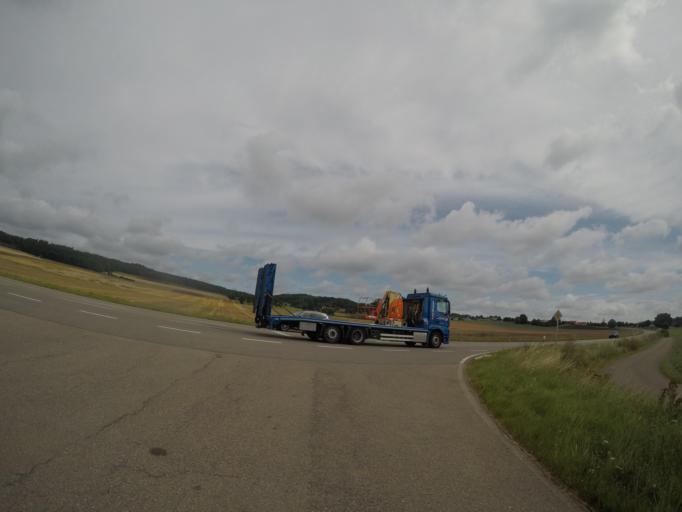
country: DE
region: Baden-Wuerttemberg
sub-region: Tuebingen Region
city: Westerheim
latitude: 48.4718
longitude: 9.6134
